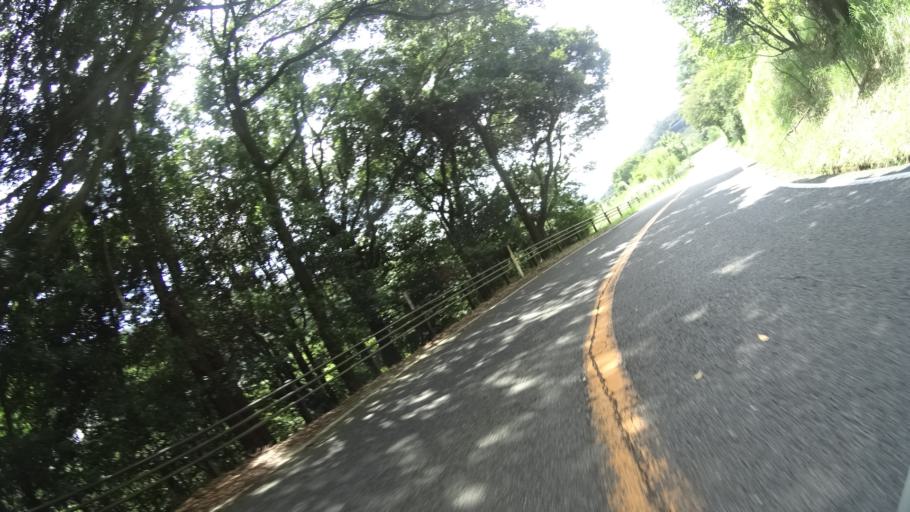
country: JP
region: Miyazaki
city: Kobayashi
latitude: 31.8992
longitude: 130.8371
